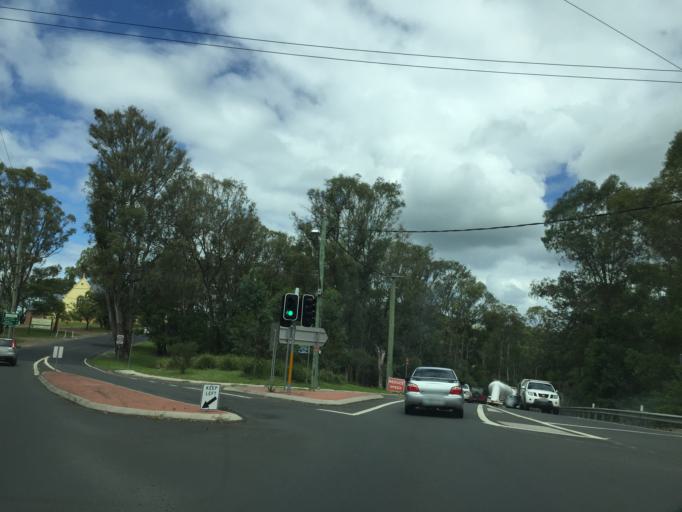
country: AU
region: New South Wales
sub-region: Hawkesbury
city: Richmond
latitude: -33.5488
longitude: 150.6742
